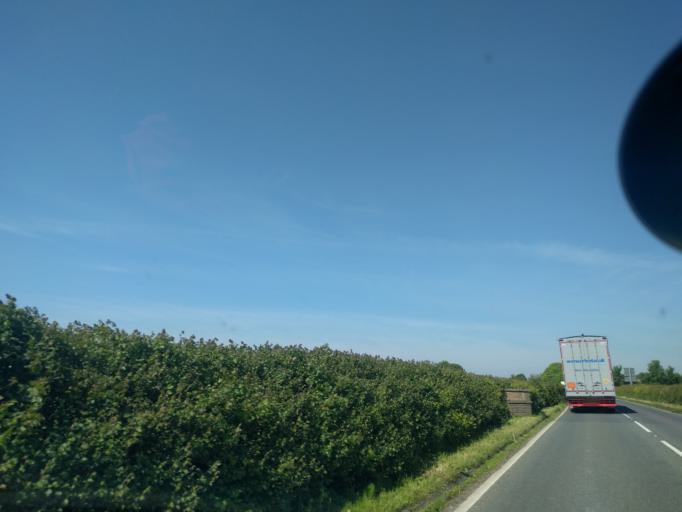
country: GB
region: England
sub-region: Somerset
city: Martock
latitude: 51.0286
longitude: -2.7529
